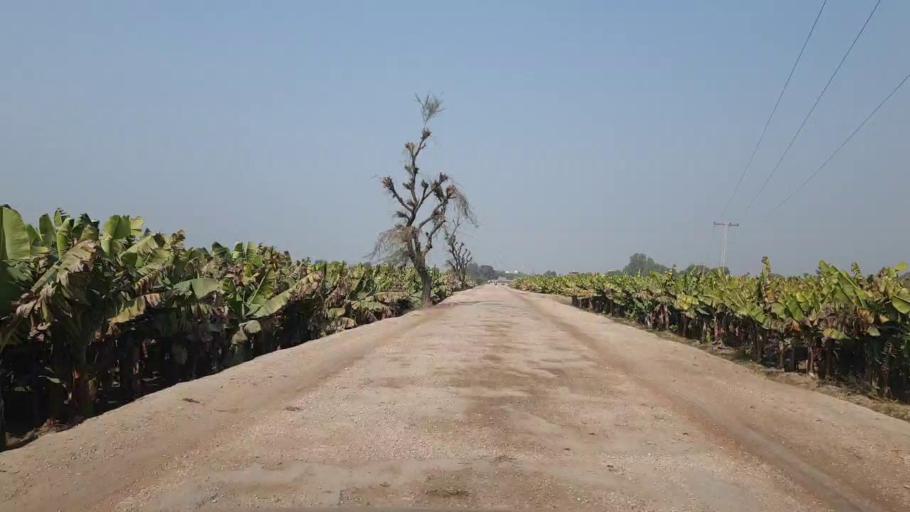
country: PK
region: Sindh
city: Bhit Shah
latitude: 25.7952
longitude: 68.4977
